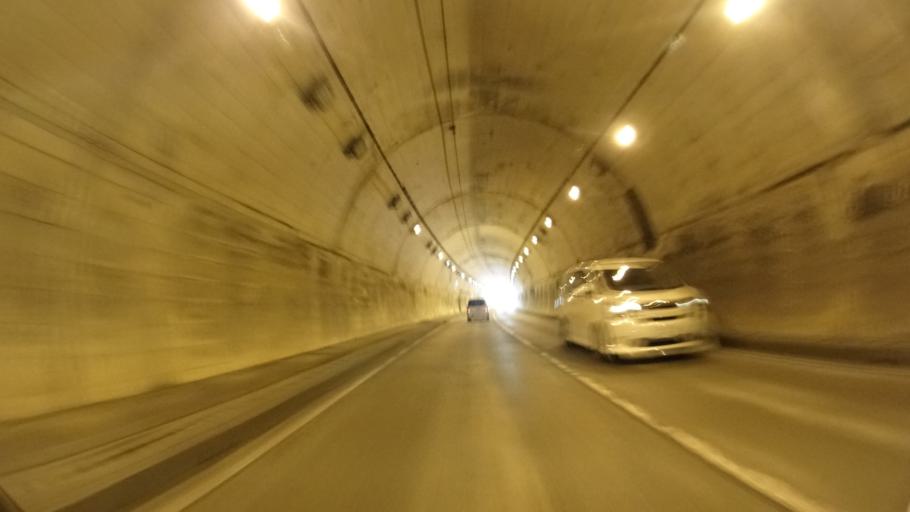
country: JP
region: Ehime
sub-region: Nishiuwa-gun
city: Ikata-cho
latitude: 33.4831
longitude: 132.3245
